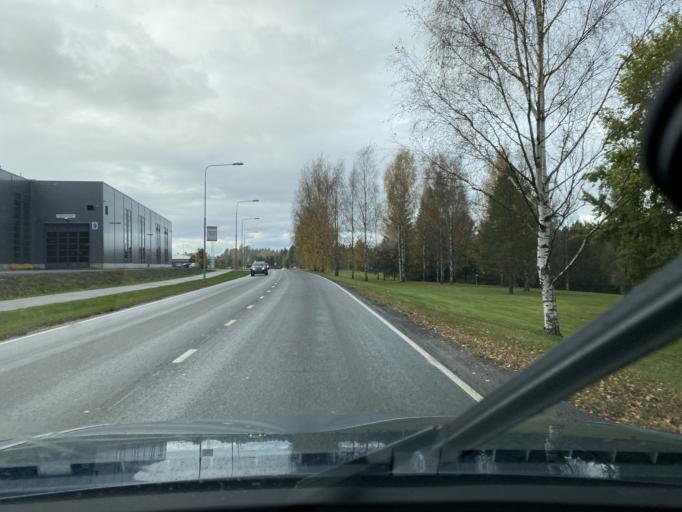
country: FI
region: Haeme
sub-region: Forssa
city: Forssa
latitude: 60.8234
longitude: 23.6029
